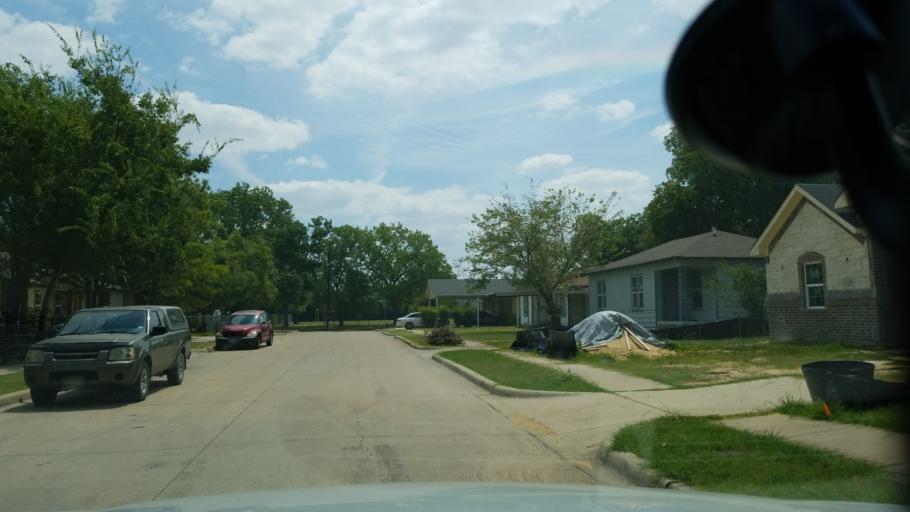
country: US
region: Texas
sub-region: Dallas County
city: Grand Prairie
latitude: 32.7521
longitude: -96.9822
